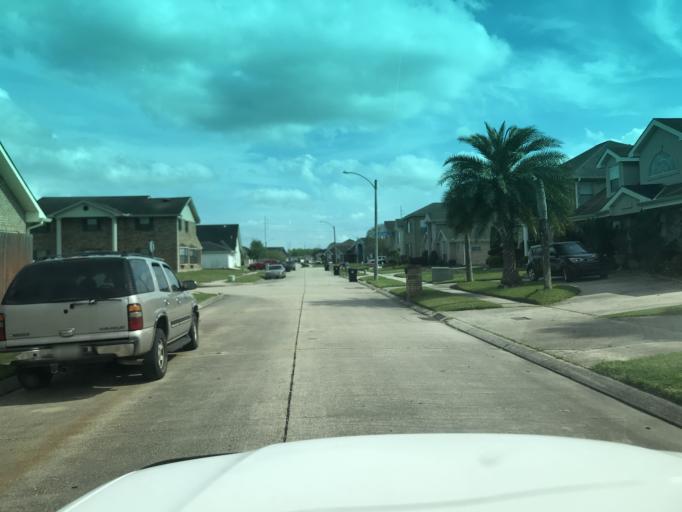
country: US
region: Louisiana
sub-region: Saint Bernard Parish
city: Chalmette
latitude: 30.0312
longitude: -89.9531
